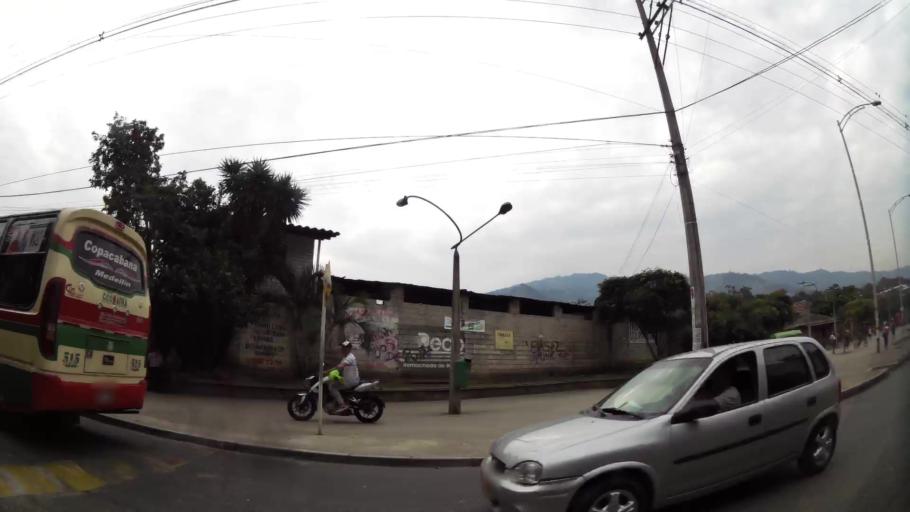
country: CO
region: Antioquia
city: Bello
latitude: 6.2981
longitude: -75.5578
